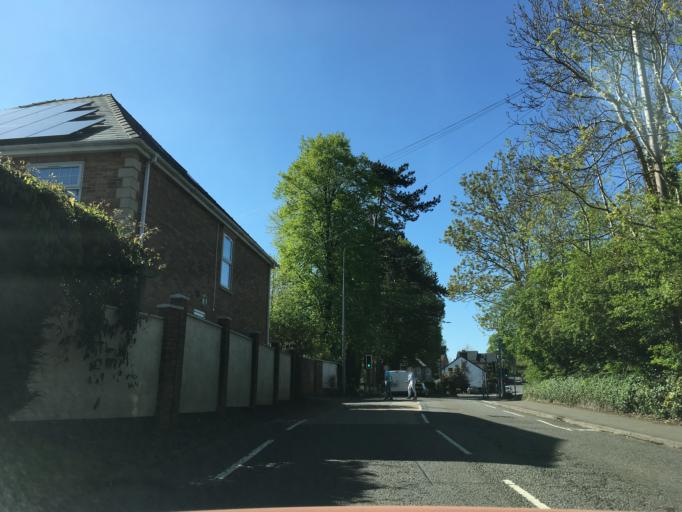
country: GB
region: Wales
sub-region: Cardiff
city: Radyr
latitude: 51.5225
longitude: -3.2357
